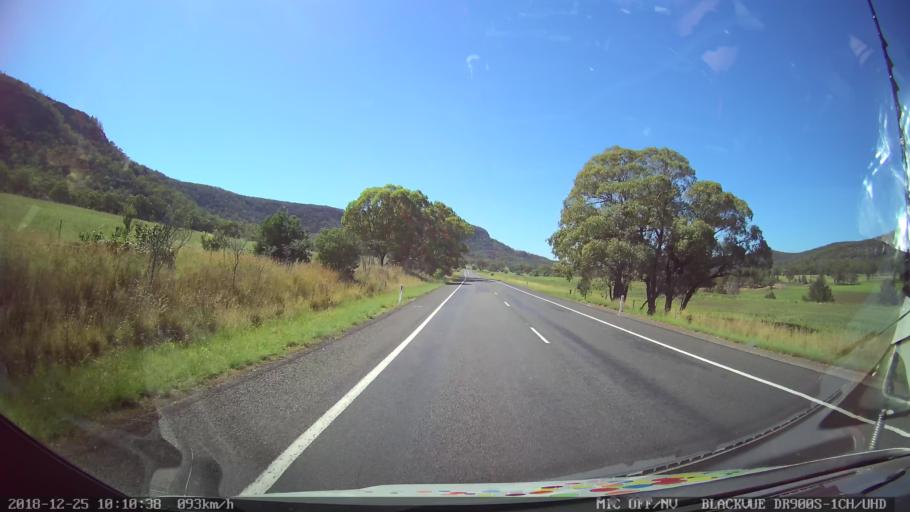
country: AU
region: New South Wales
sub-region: Muswellbrook
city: Denman
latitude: -32.3062
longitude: 150.5238
